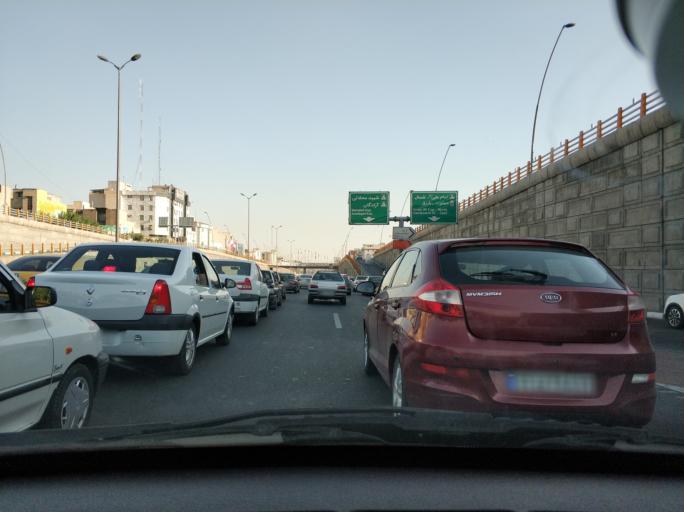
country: IR
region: Tehran
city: Tehran
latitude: 35.7039
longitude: 51.4575
